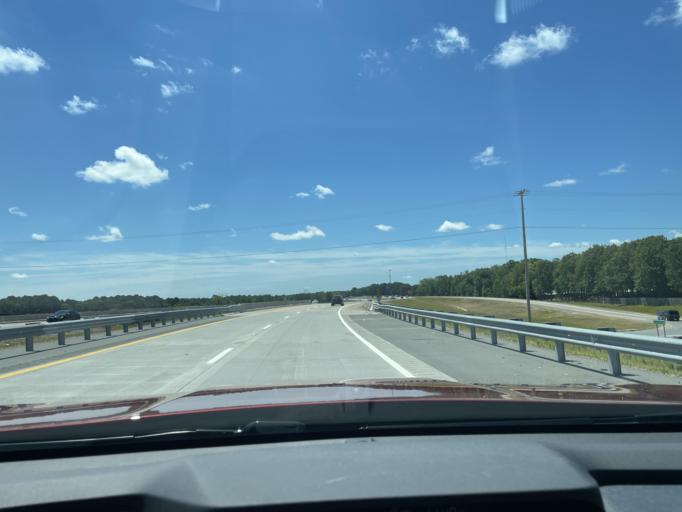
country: US
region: Arkansas
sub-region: Jefferson County
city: White Hall
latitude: 34.2286
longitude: -92.0788
